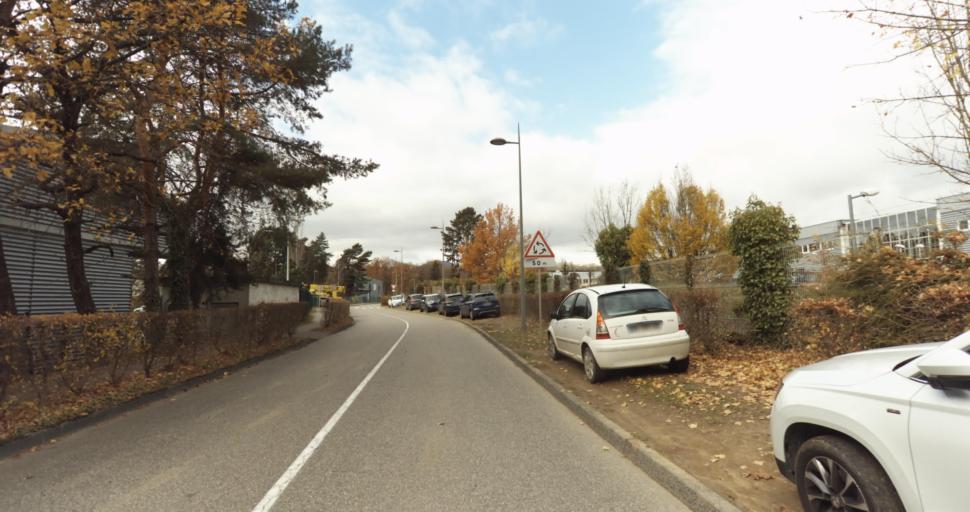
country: FR
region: Rhone-Alpes
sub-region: Departement de la Haute-Savoie
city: Metz-Tessy
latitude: 45.9290
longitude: 6.1171
